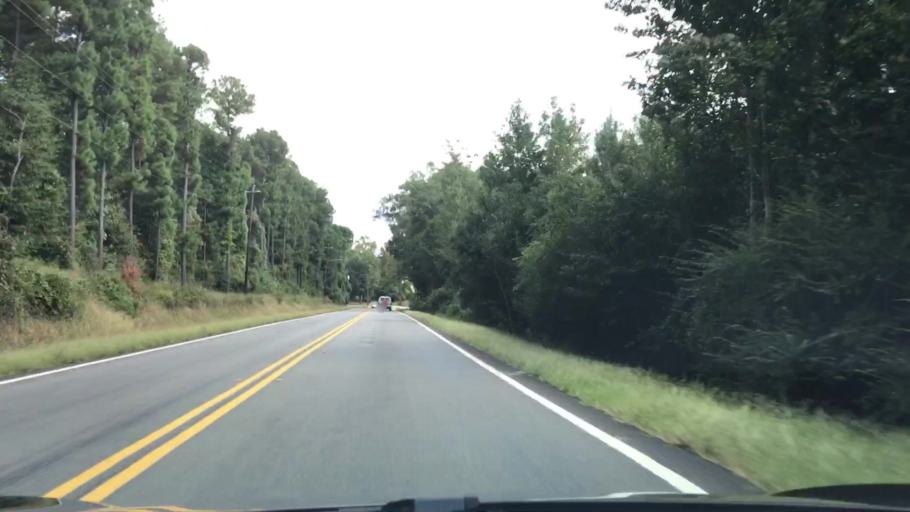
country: US
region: Georgia
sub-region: Greene County
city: Union Point
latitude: 33.5396
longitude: -83.0902
